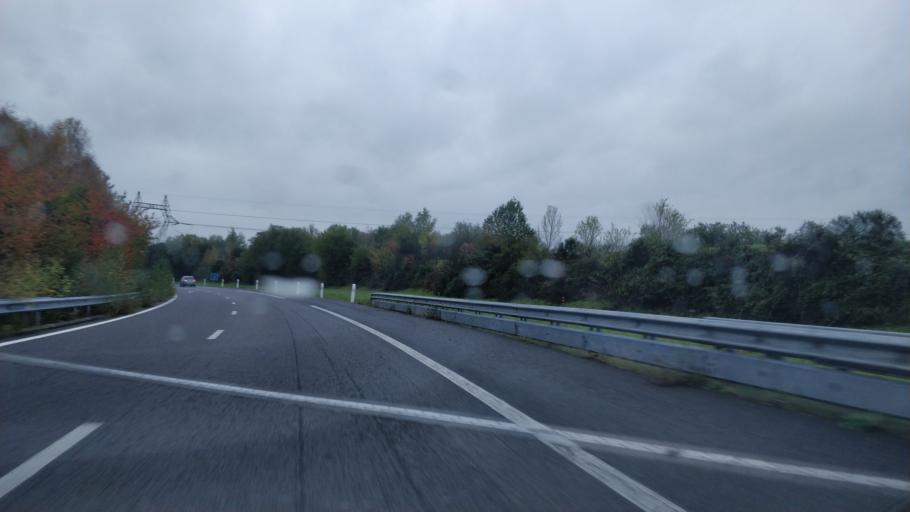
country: FR
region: Brittany
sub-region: Departement d'Ille-et-Vilaine
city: Fouillard
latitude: 48.1491
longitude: -1.5984
